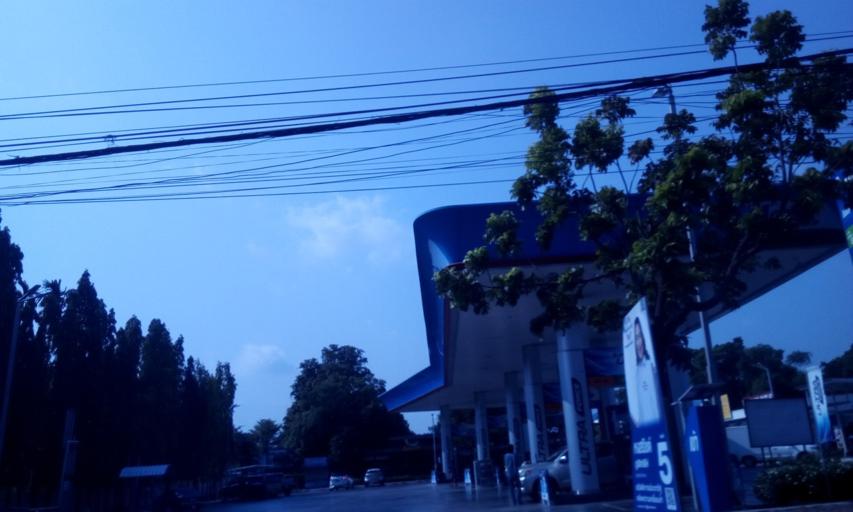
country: TH
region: Bangkok
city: Sai Mai
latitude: 13.9321
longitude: 100.6564
